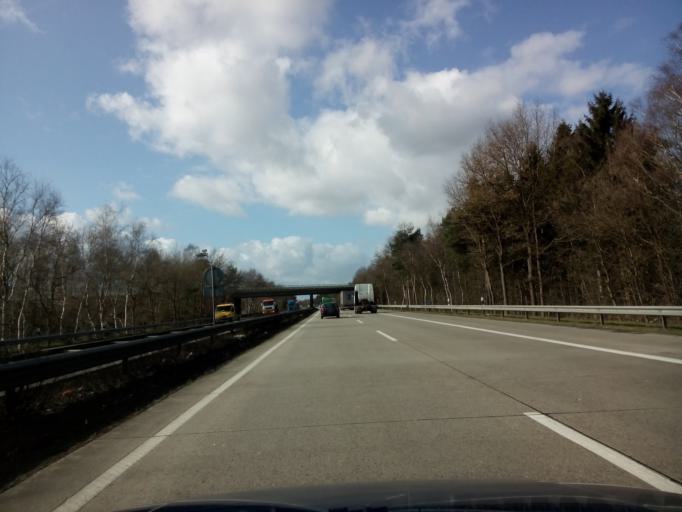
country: DE
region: Lower Saxony
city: Dotlingen
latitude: 52.9136
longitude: 8.3957
